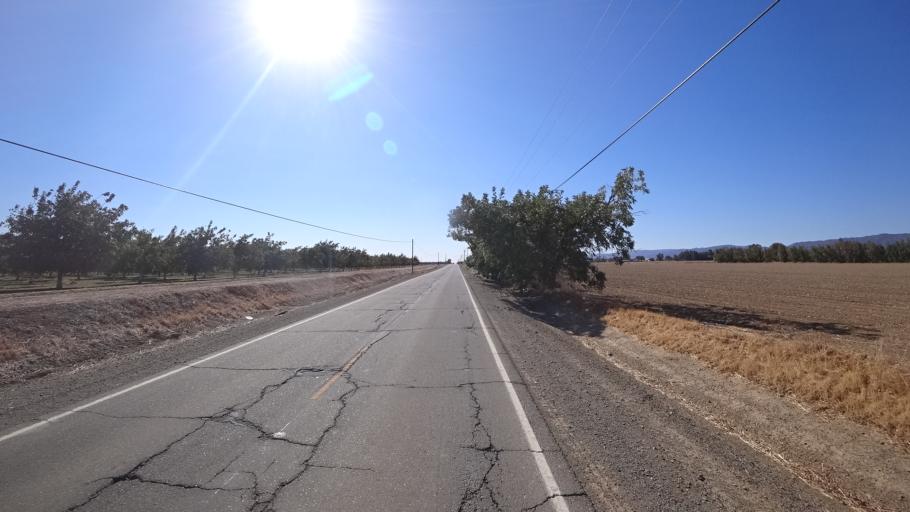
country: US
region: California
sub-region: Yolo County
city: Cottonwood
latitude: 38.5943
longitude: -121.9715
